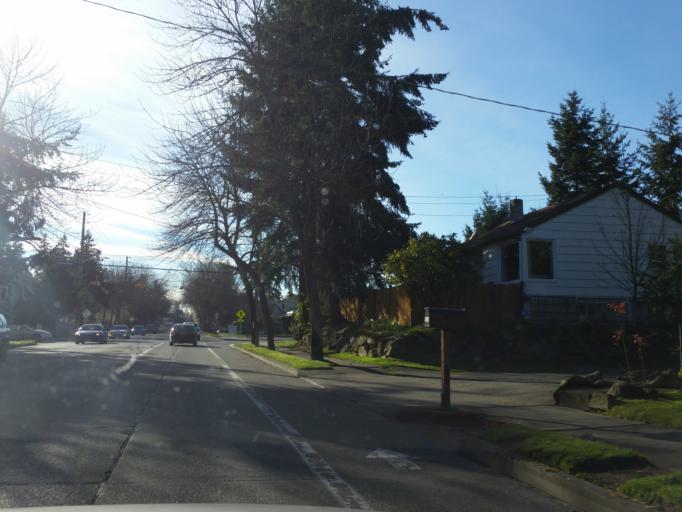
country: US
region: Washington
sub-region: King County
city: Shoreline
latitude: 47.7633
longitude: -122.3395
